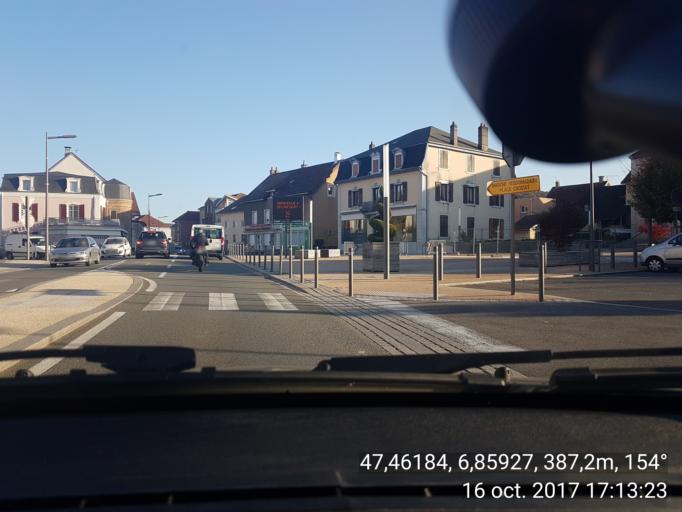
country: FR
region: Franche-Comte
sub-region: Departement du Doubs
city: Seloncourt
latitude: 47.4618
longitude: 6.8593
